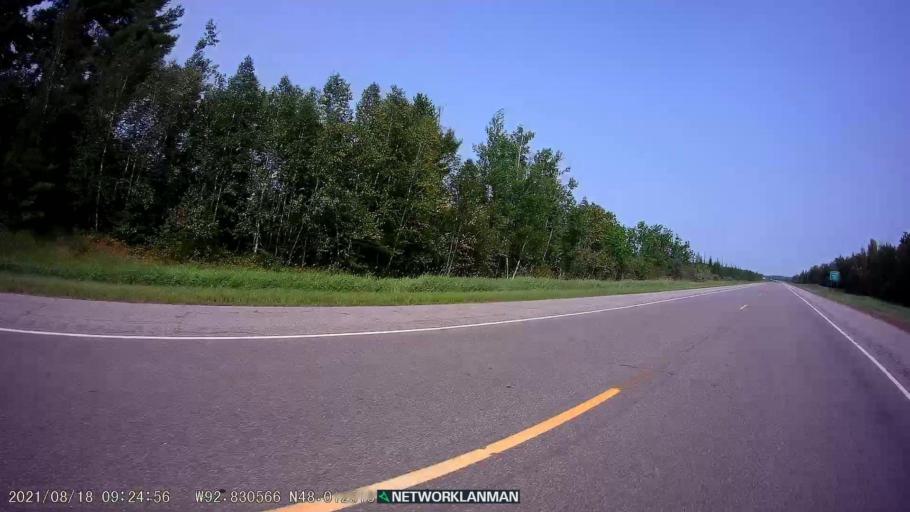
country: US
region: Minnesota
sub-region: Saint Louis County
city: Mountain Iron
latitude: 48.0130
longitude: -92.8309
